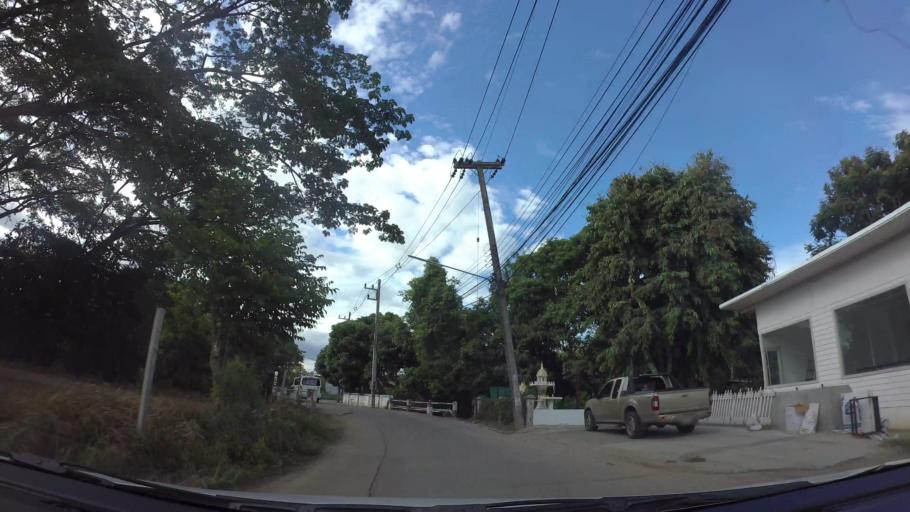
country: TH
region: Chiang Mai
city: Saraphi
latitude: 18.7498
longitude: 99.0290
